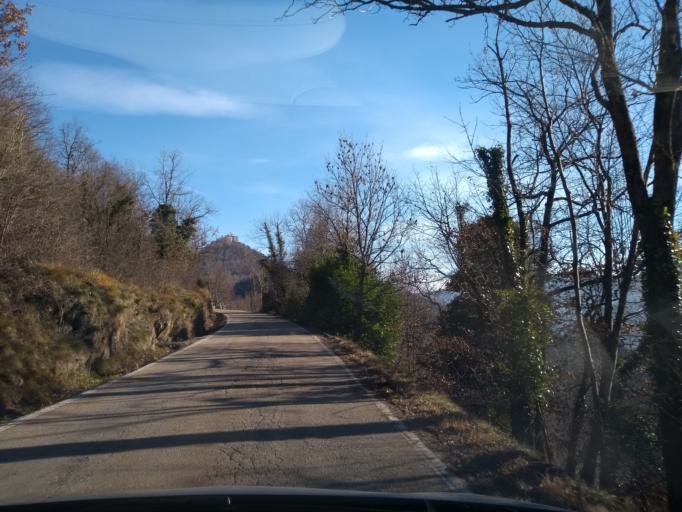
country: IT
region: Piedmont
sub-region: Provincia di Torino
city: Pessinetto
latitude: 45.2829
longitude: 7.4244
